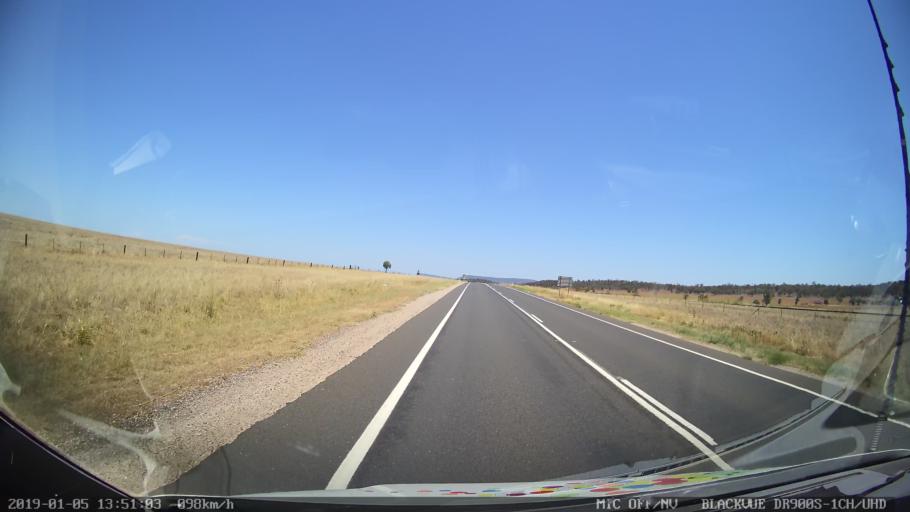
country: AU
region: New South Wales
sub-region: Gunnedah
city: Gunnedah
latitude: -31.0390
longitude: 150.2761
